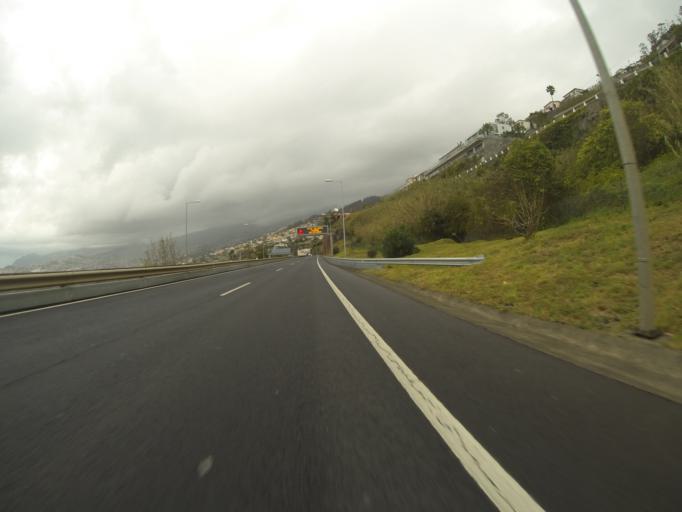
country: PT
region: Madeira
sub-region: Funchal
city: Nossa Senhora do Monte
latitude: 32.6513
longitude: -16.8759
